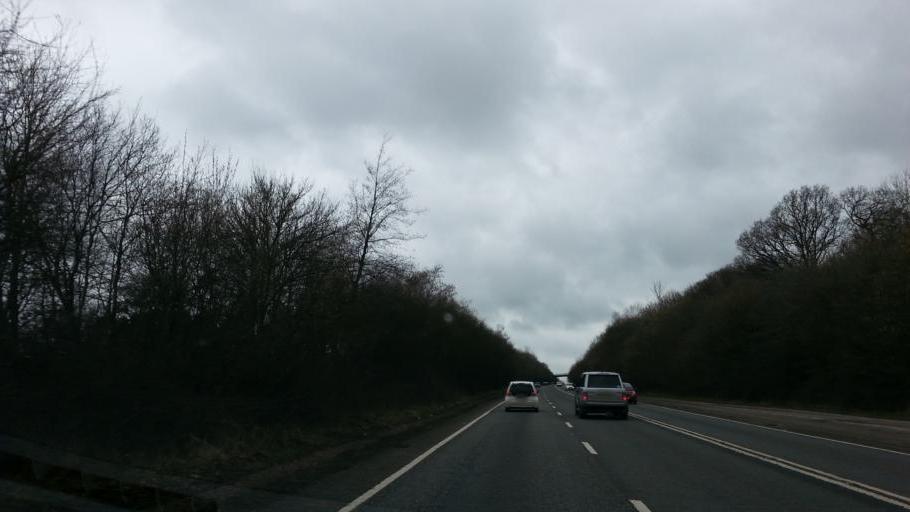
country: GB
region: England
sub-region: Devon
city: South Molton
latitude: 51.0175
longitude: -3.7937
